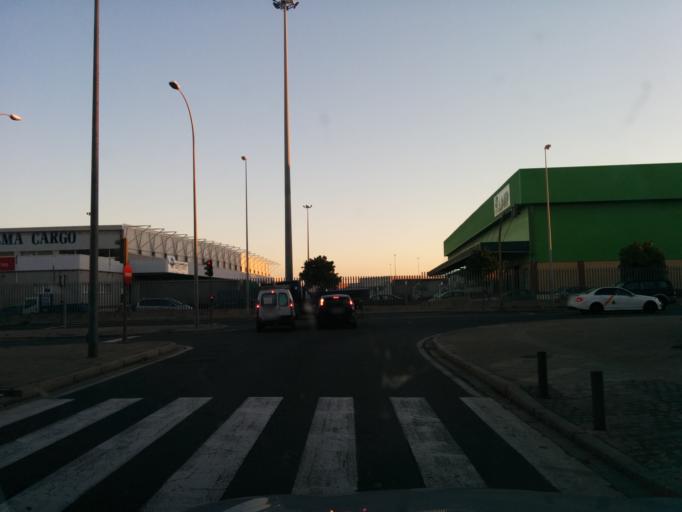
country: ES
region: Andalusia
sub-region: Provincia de Sevilla
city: Sevilla
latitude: 37.3812
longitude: -5.9390
